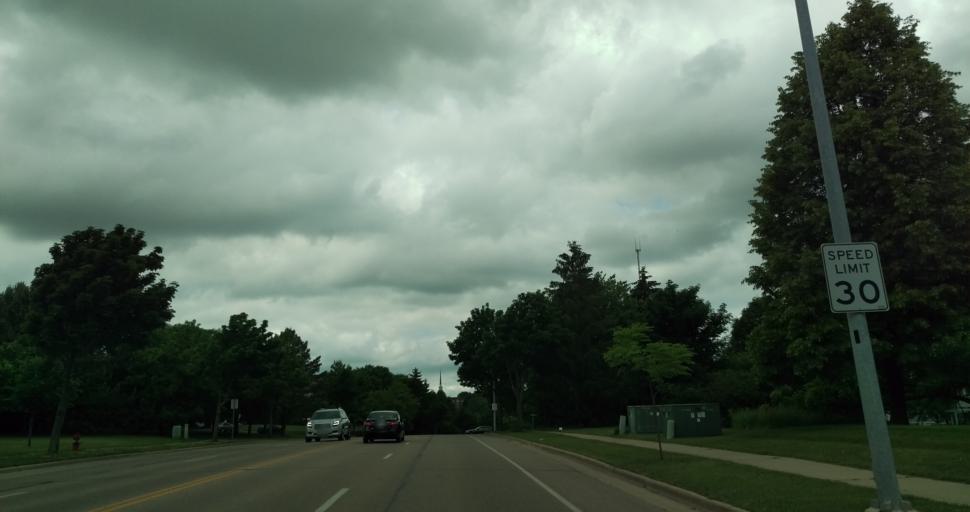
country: US
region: Wisconsin
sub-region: Dane County
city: Middleton
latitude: 43.0510
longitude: -89.5124
